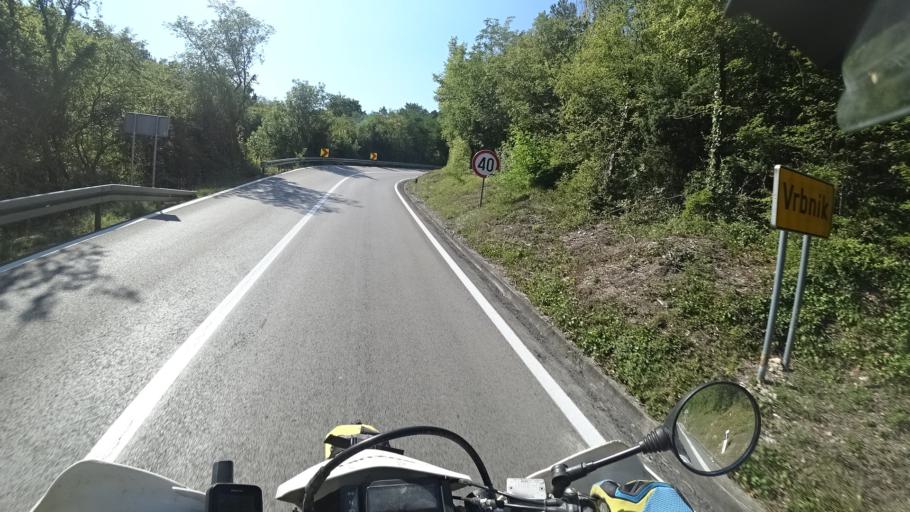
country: HR
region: Sibensko-Kniniska
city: Knin
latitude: 44.0172
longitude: 16.1957
